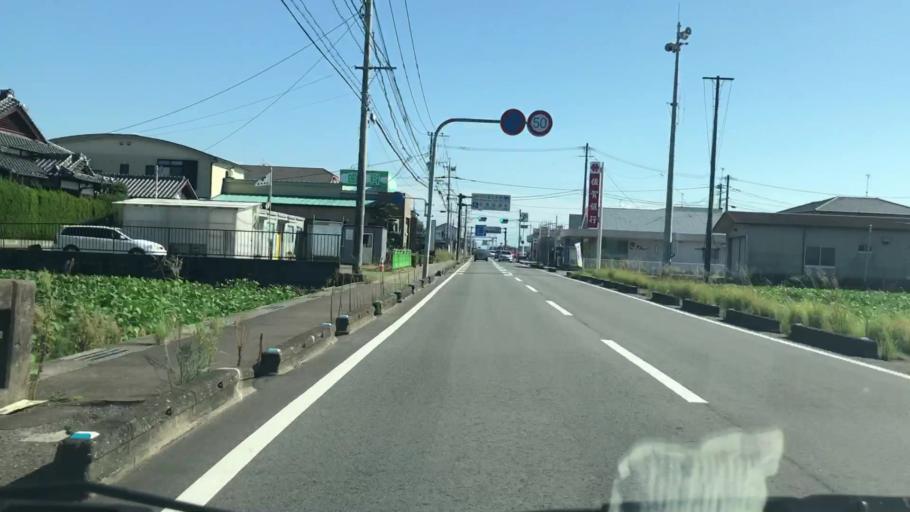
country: JP
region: Saga Prefecture
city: Okawa
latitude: 33.2075
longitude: 130.3353
